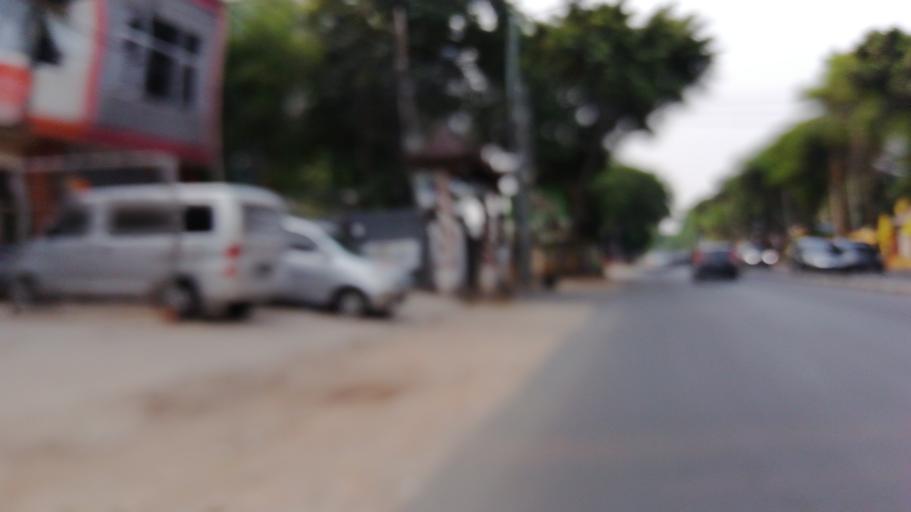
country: ID
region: Jakarta Raya
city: Jakarta
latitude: -6.2856
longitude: 106.8071
